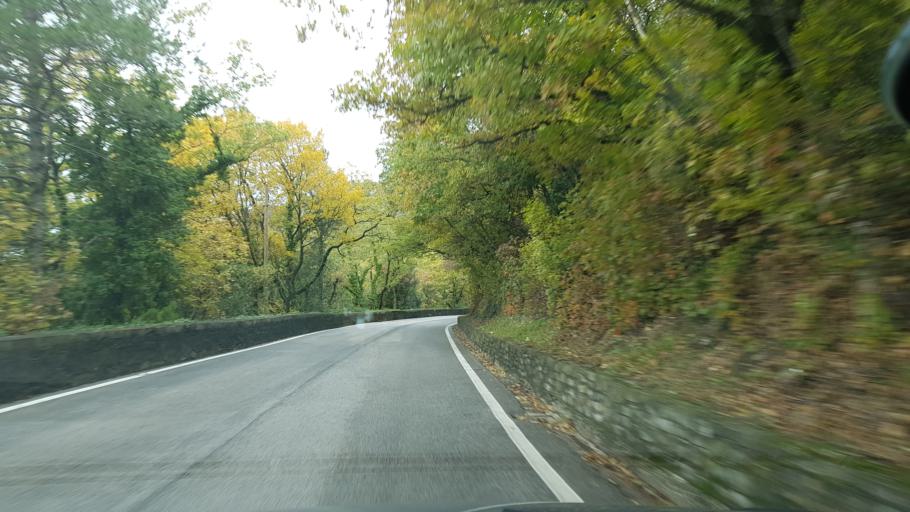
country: IT
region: Friuli Venezia Giulia
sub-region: Provincia di Trieste
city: Prosecco-Contovello
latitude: 45.6920
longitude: 13.7444
